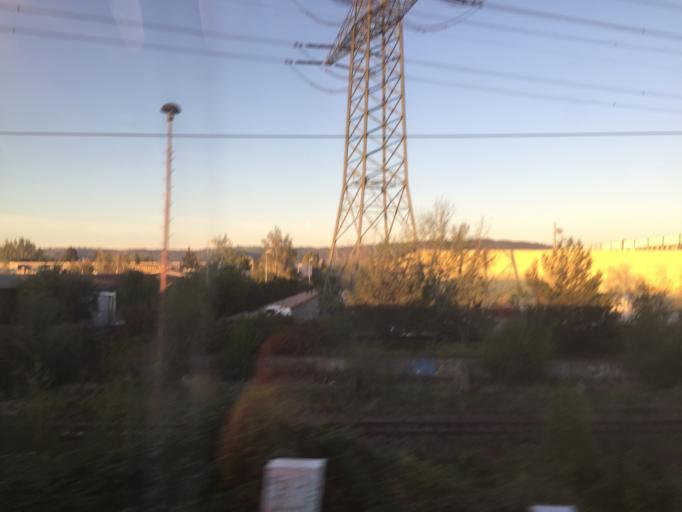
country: DE
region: Saxony
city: Heidenau
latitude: 50.9880
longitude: 13.8478
